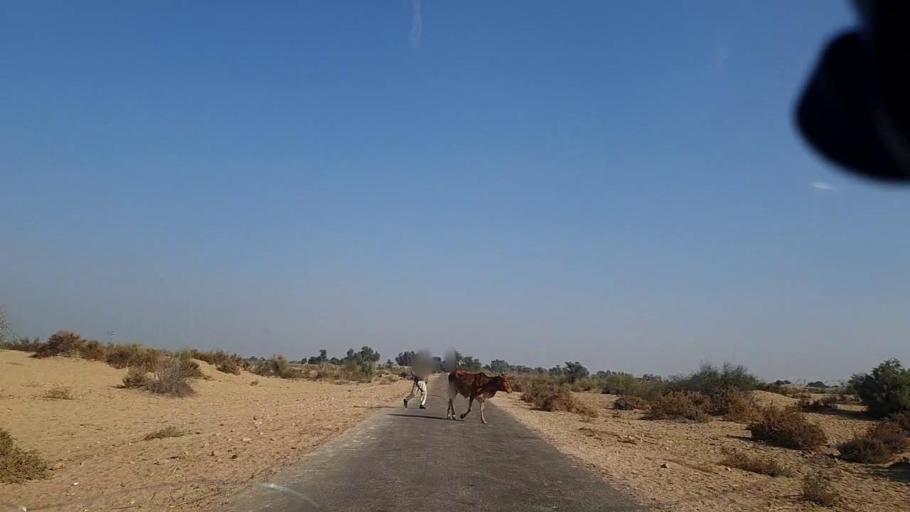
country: PK
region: Sindh
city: Khanpur
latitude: 27.6863
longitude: 69.4799
